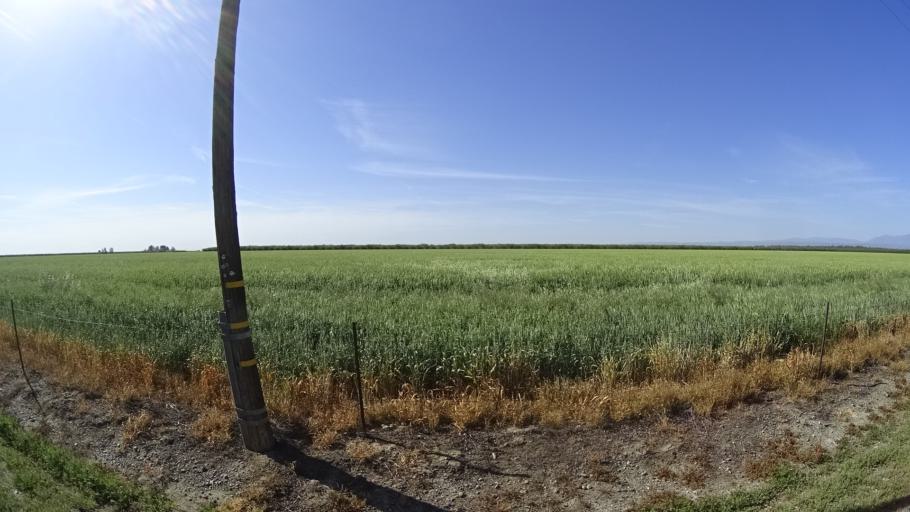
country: US
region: California
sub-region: Glenn County
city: Willows
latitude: 39.6112
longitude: -122.1619
